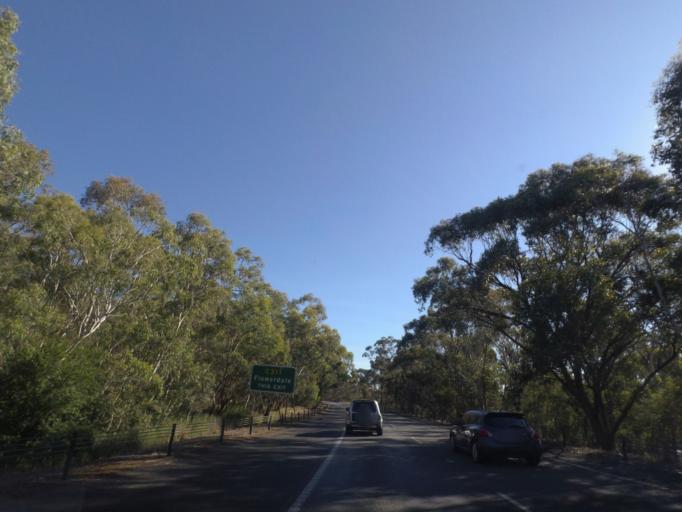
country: AU
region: Victoria
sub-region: Murrindindi
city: Kinglake West
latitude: -37.1773
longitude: 145.0711
